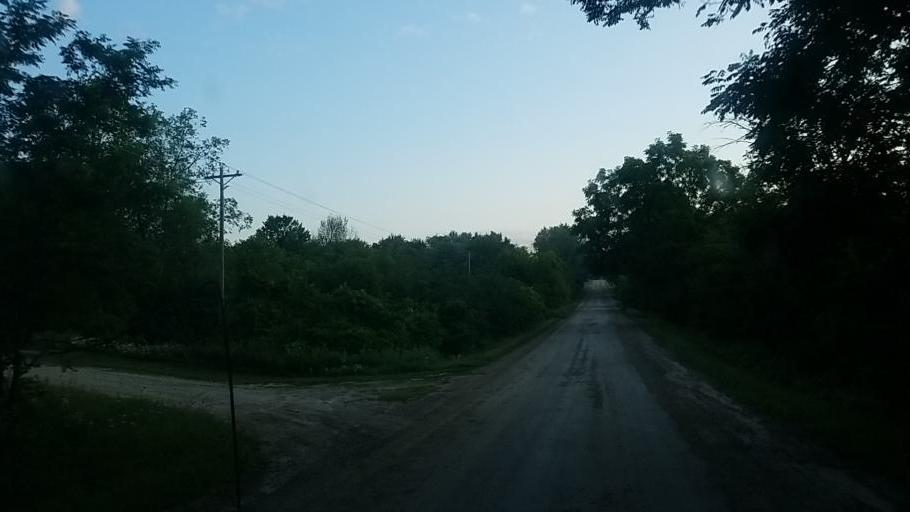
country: US
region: Michigan
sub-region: Osceola County
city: Evart
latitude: 43.9095
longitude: -85.2066
